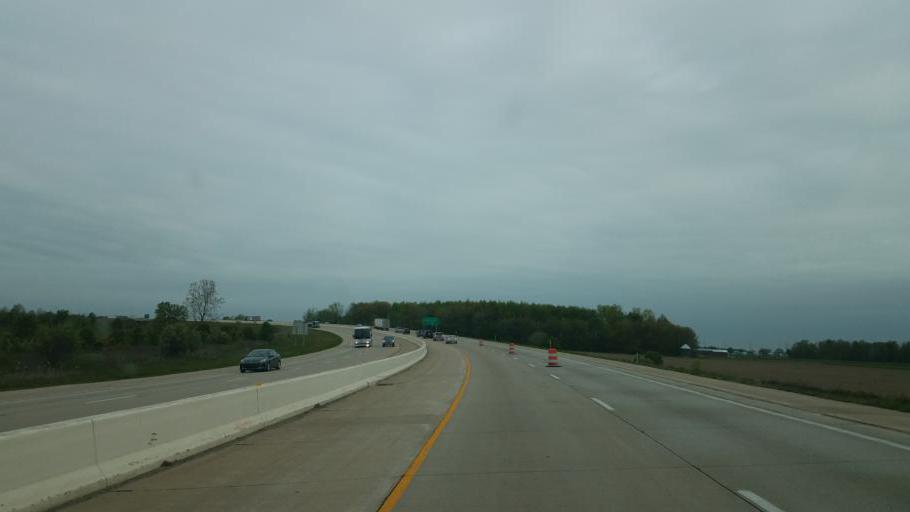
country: US
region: Indiana
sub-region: Allen County
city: New Haven
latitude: 41.1236
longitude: -84.9956
